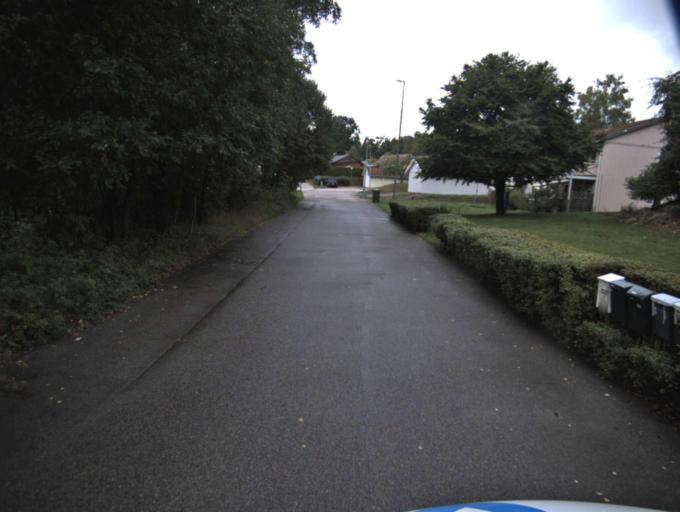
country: SE
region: Vaestra Goetaland
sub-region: Tranemo Kommun
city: Langhem
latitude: 57.6983
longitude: 13.3025
